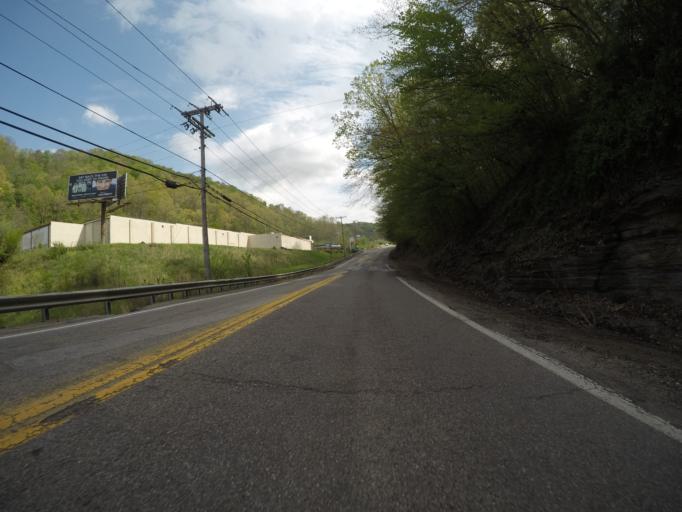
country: US
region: West Virginia
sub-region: Boone County
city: Madison
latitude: 38.0870
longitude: -81.8389
